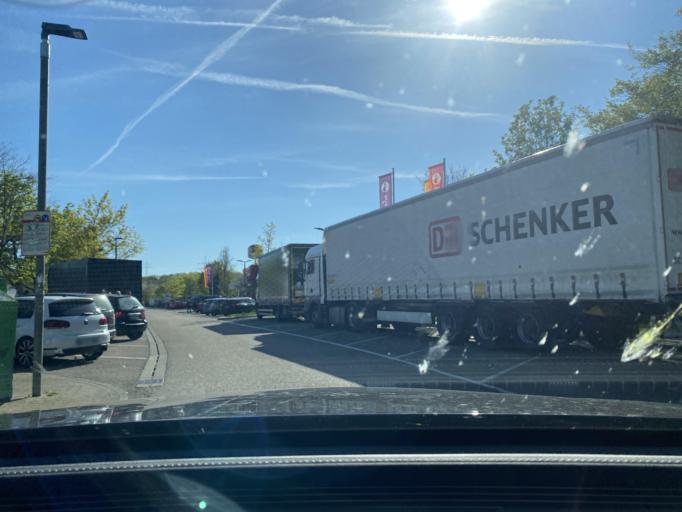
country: DE
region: Baden-Wuerttemberg
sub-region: Regierungsbezirk Stuttgart
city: Ilsfeld
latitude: 49.0454
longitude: 9.2633
